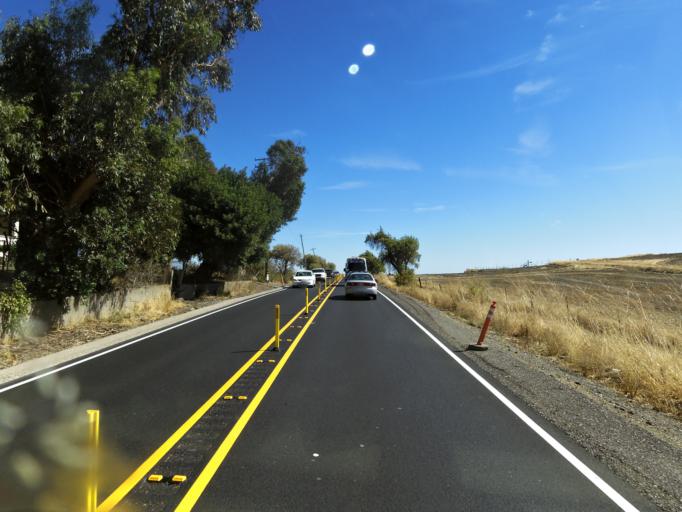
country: US
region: California
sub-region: Solano County
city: Rio Vista
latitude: 38.1738
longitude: -121.7134
